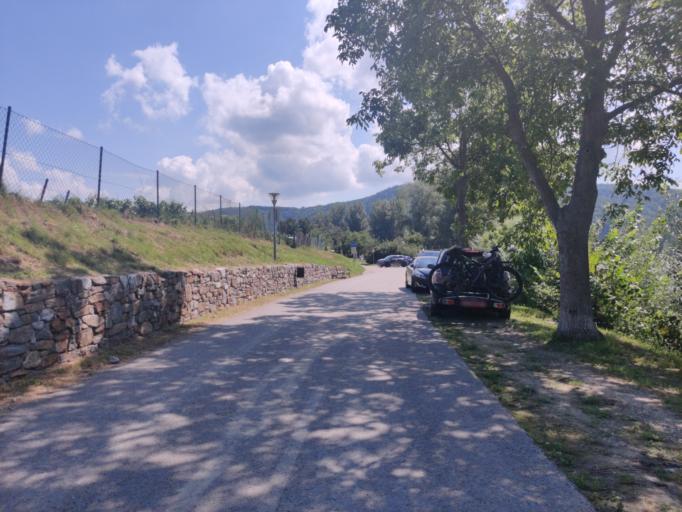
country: AT
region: Lower Austria
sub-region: Politischer Bezirk Krems
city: Durnstein
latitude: 48.3919
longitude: 15.5210
